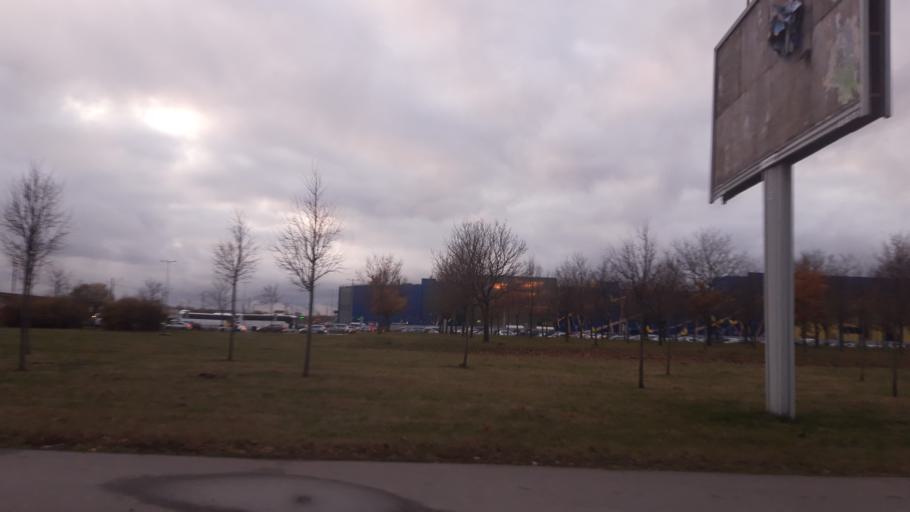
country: RU
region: St.-Petersburg
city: Kupchino
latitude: 59.8185
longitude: 30.3226
